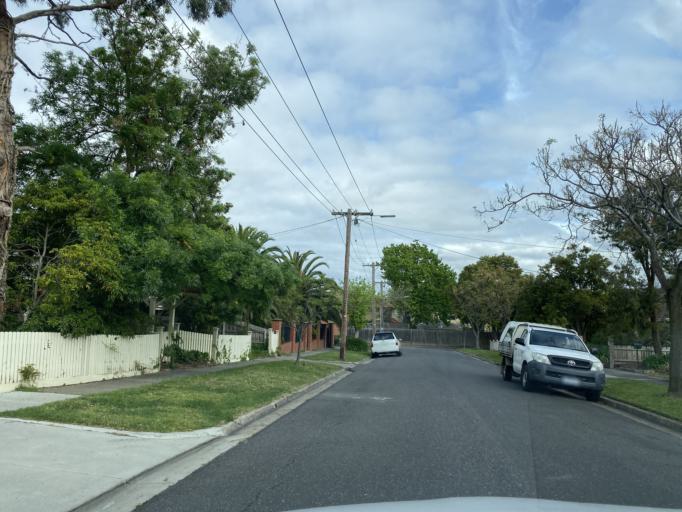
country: AU
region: Victoria
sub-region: Boroondara
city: Camberwell
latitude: -37.8455
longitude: 145.0867
